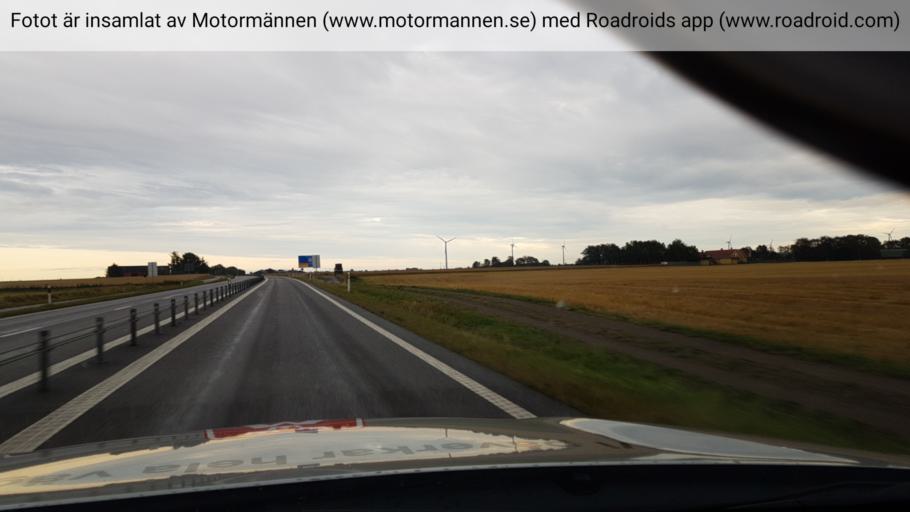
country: SE
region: Halland
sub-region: Laholms Kommun
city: Mellbystrand
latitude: 56.5041
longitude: 12.9680
